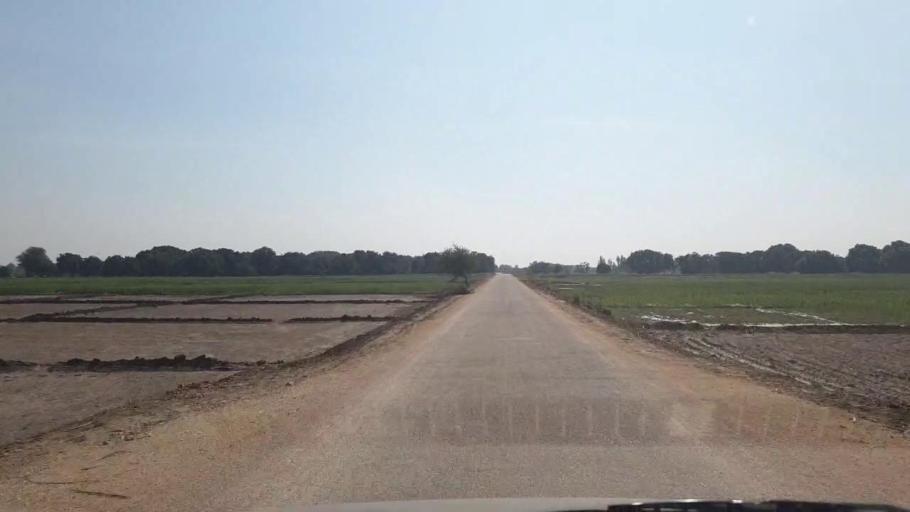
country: PK
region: Sindh
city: Chambar
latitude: 25.3812
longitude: 68.8049
